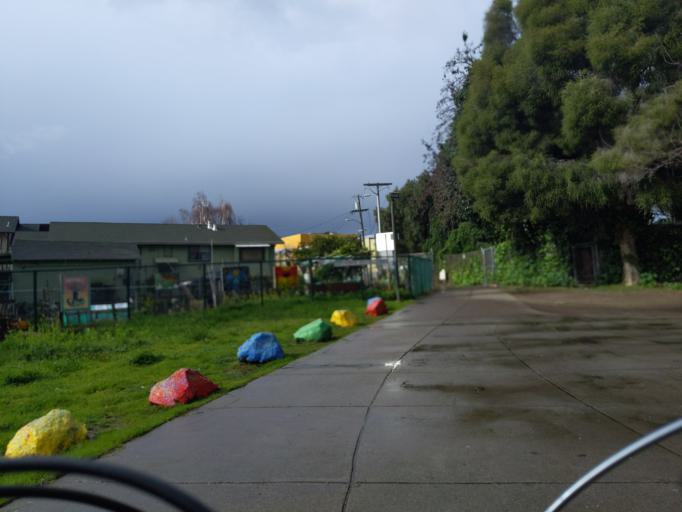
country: US
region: California
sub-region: Alameda County
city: Alameda
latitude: 37.7810
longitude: -122.2259
